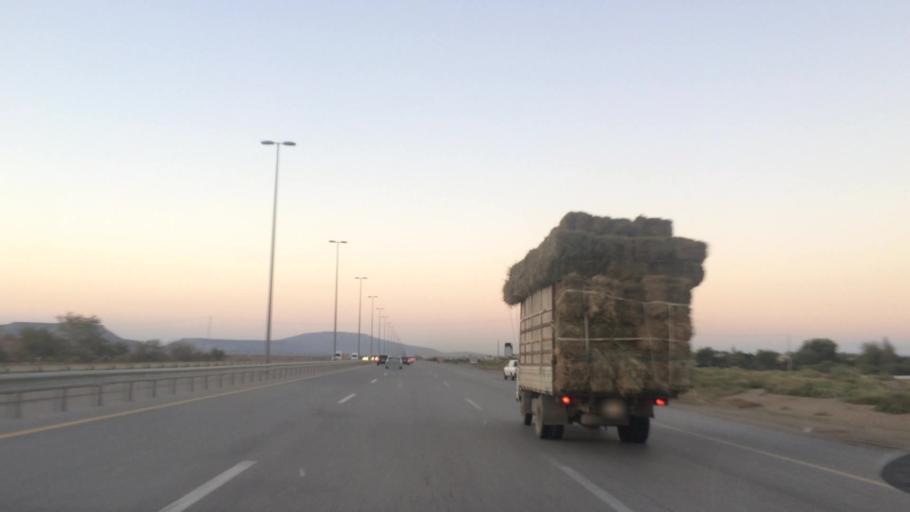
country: AZ
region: Baki
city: Qobustan
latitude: 40.0203
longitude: 49.4251
